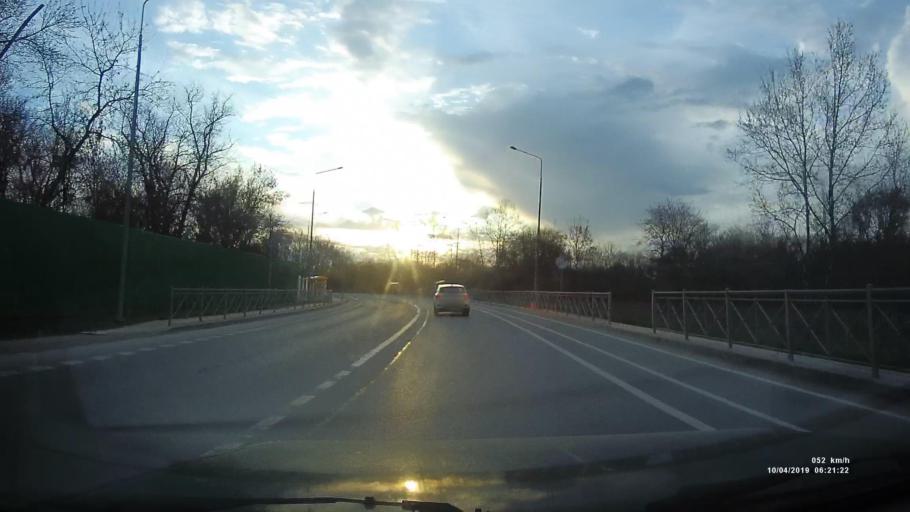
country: RU
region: Rostov
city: Bataysk
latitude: 47.1987
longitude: 39.7917
